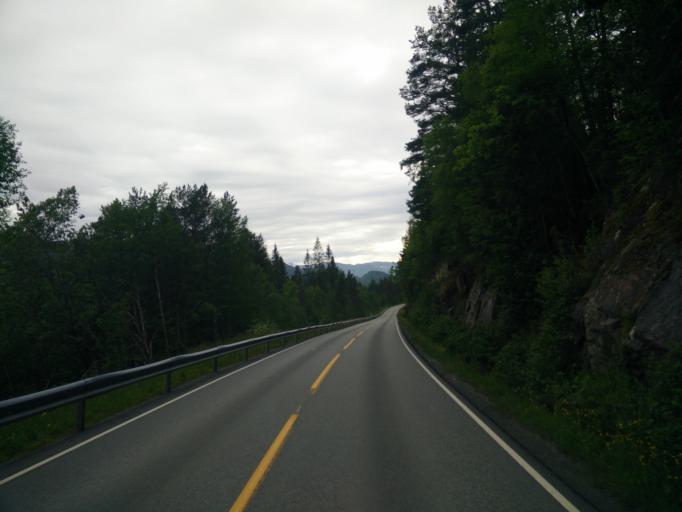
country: NO
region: Sor-Trondelag
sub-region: Hemne
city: Kyrksaeterora
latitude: 63.2143
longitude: 9.1091
